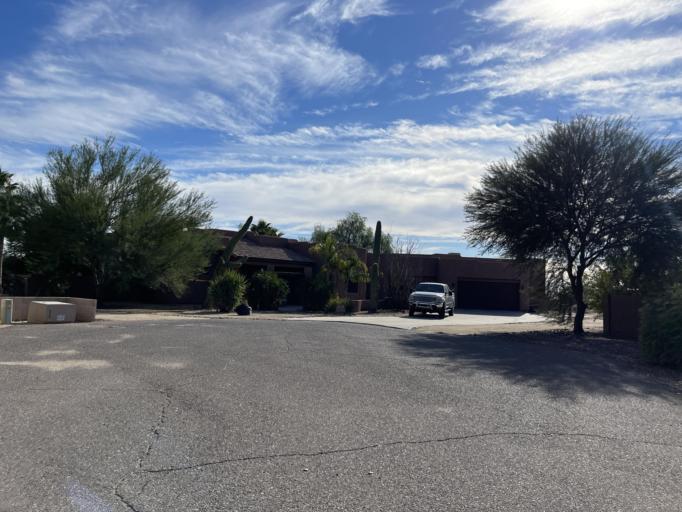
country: US
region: Arizona
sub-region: Maricopa County
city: Anthem
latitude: 33.8378
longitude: -112.0736
